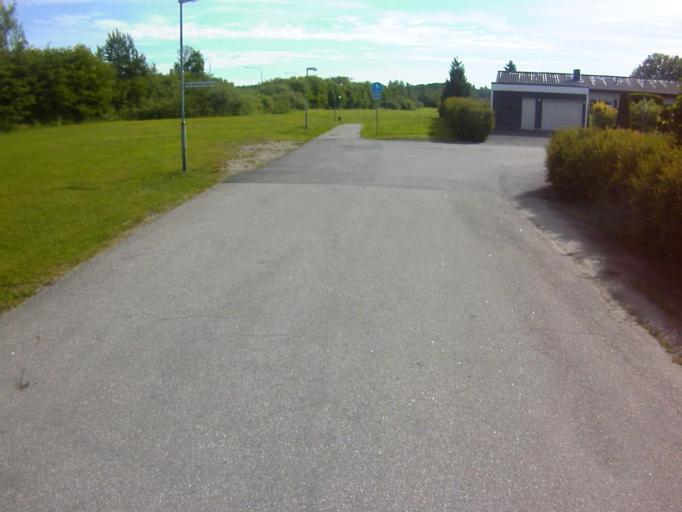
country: SE
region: Soedermanland
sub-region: Eskilstuna Kommun
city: Skogstorp
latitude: 59.3521
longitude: 16.4488
